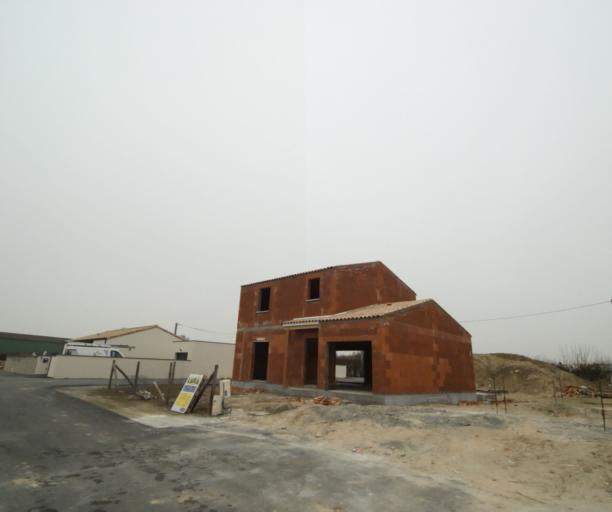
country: FR
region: Poitou-Charentes
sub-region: Departement des Deux-Sevres
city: Bessines
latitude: 46.2969
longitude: -0.4956
